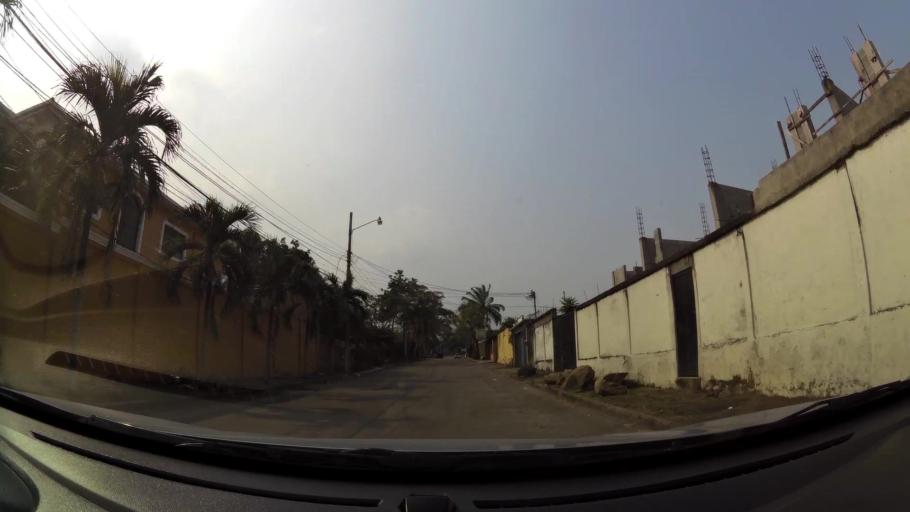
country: HN
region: Cortes
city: Armenta
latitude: 15.4957
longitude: -88.0441
